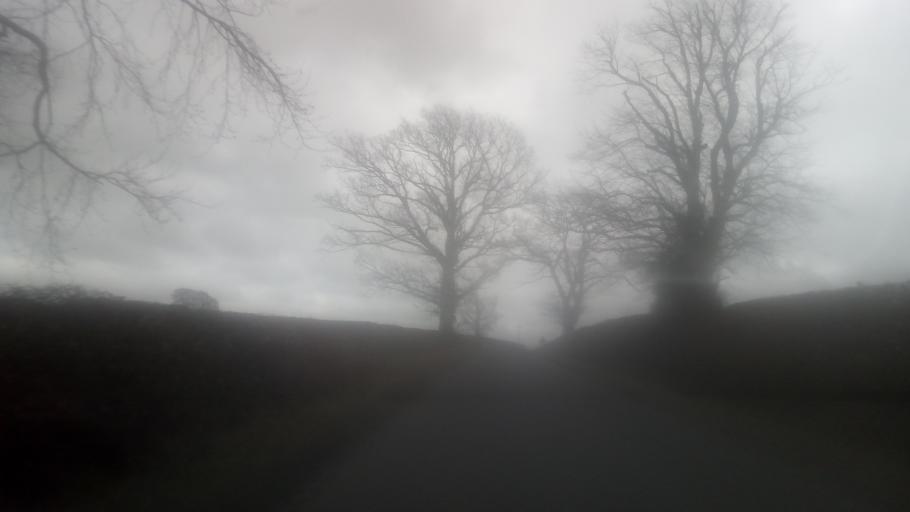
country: GB
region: Scotland
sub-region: The Scottish Borders
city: Jedburgh
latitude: 55.4691
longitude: -2.4888
